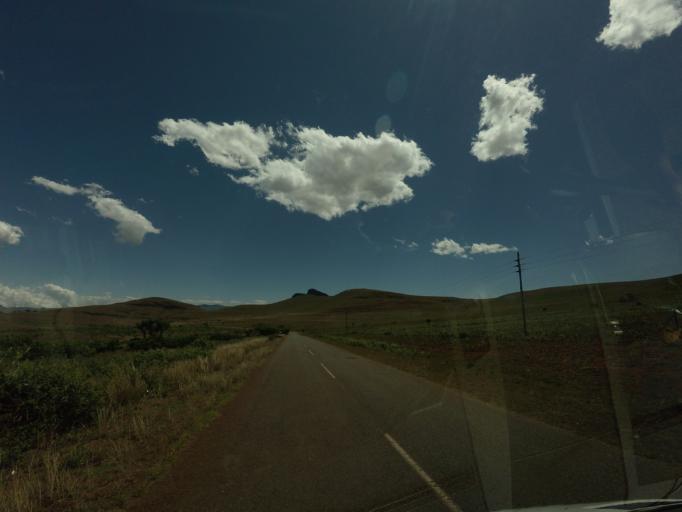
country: ZA
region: Limpopo
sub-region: Mopani District Municipality
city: Hoedspruit
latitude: -24.6224
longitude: 30.8146
